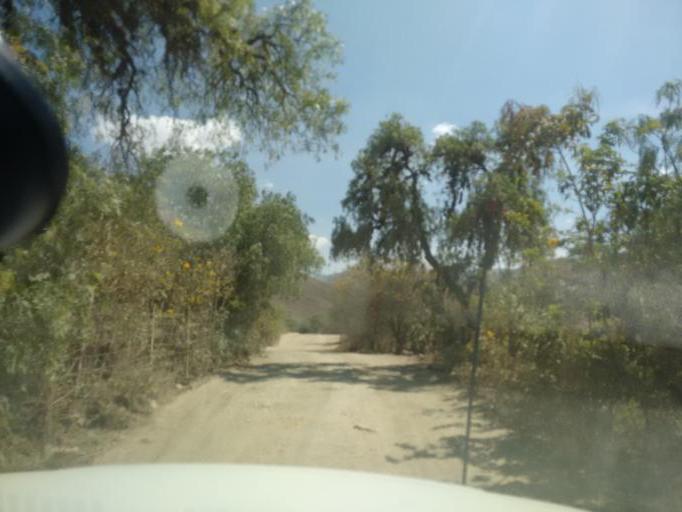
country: CO
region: Boyaca
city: Sachica
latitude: 5.5862
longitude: -73.5295
